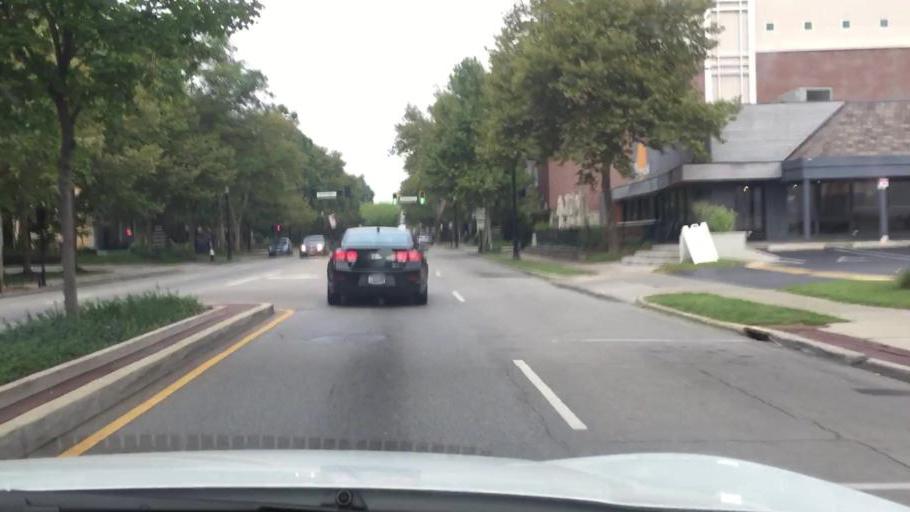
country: US
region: Ohio
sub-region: Franklin County
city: Bexley
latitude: 39.9572
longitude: -82.9349
